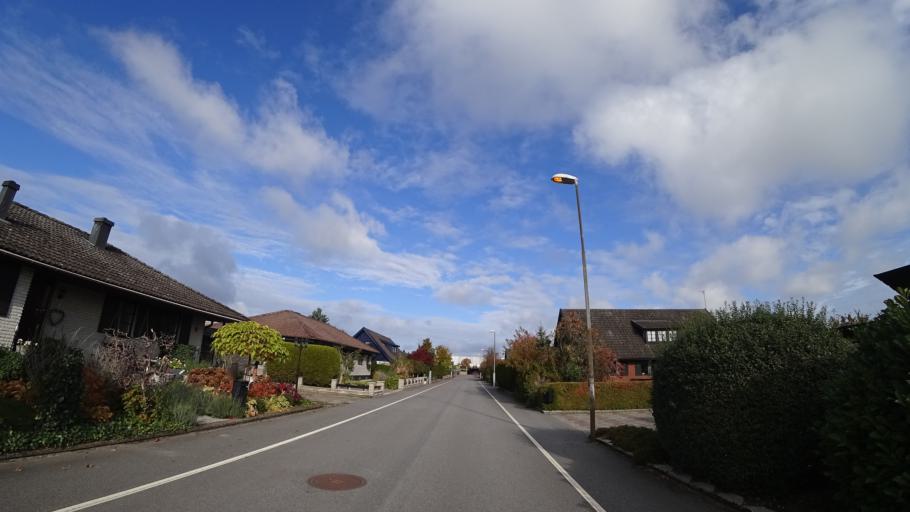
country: SE
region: Skane
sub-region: Staffanstorps Kommun
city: Staffanstorp
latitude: 55.6347
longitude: 13.1959
